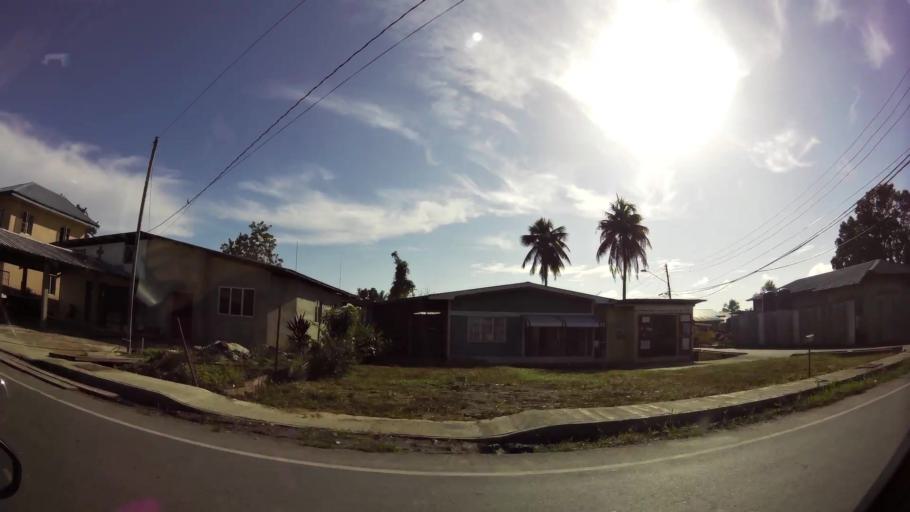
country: TT
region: Chaguanas
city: Chaguanas
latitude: 10.5258
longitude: -61.3789
